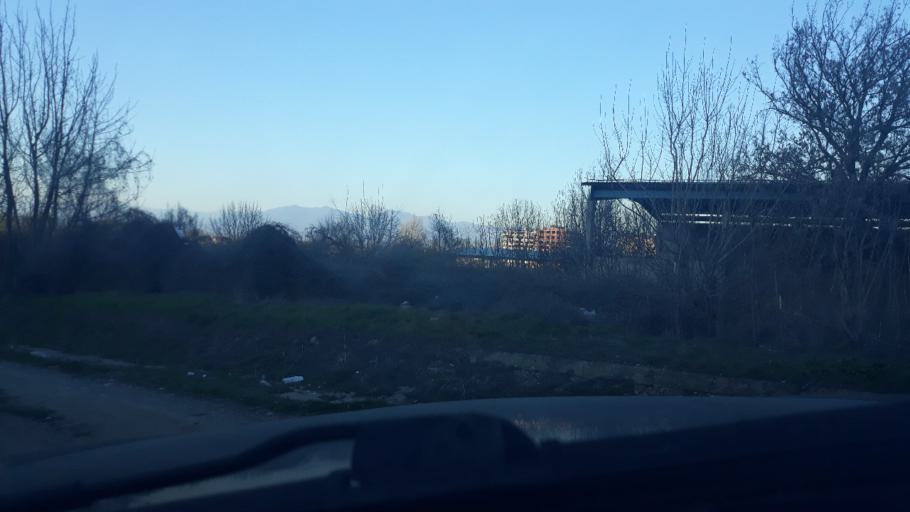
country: MK
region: Strumica
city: Strumica
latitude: 41.4398
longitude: 22.6274
